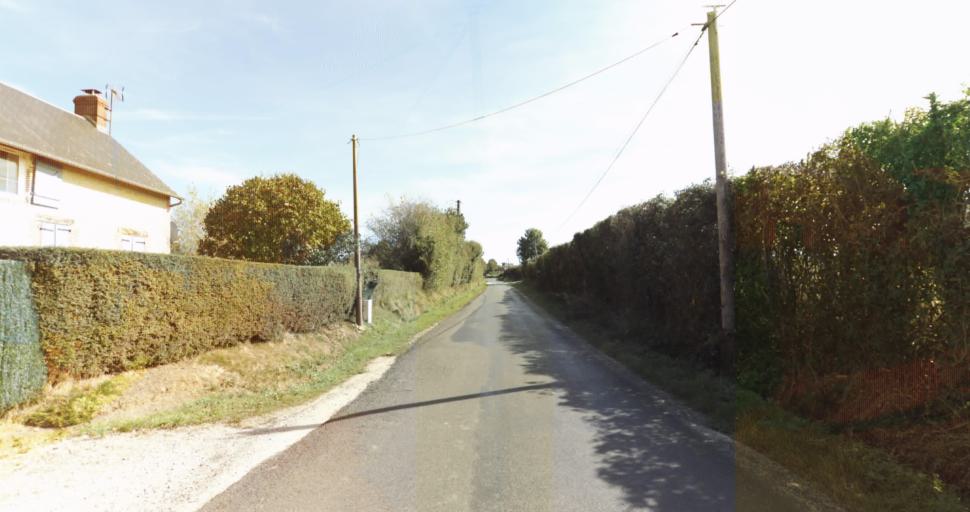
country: FR
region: Lower Normandy
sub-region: Departement de l'Orne
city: Gace
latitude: 48.7238
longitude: 0.2271
